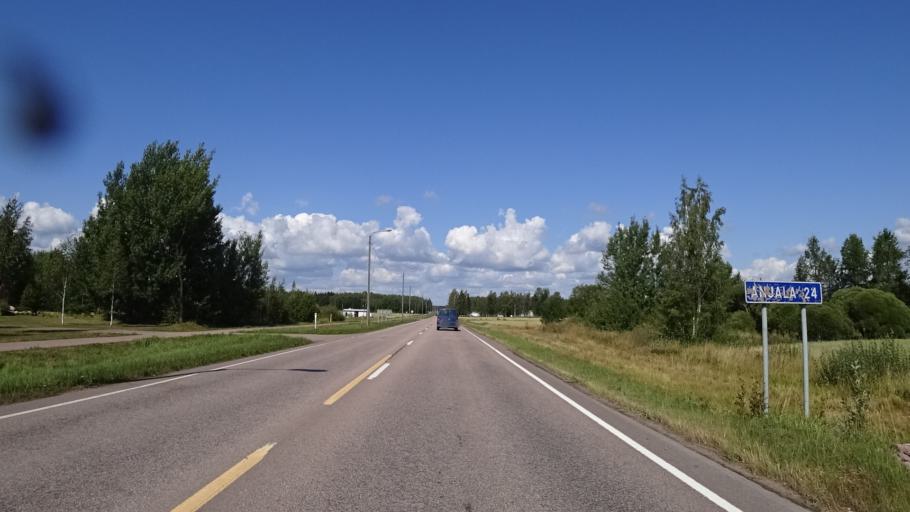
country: FI
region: Kymenlaakso
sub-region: Kotka-Hamina
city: Karhula
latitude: 60.5267
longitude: 26.9425
